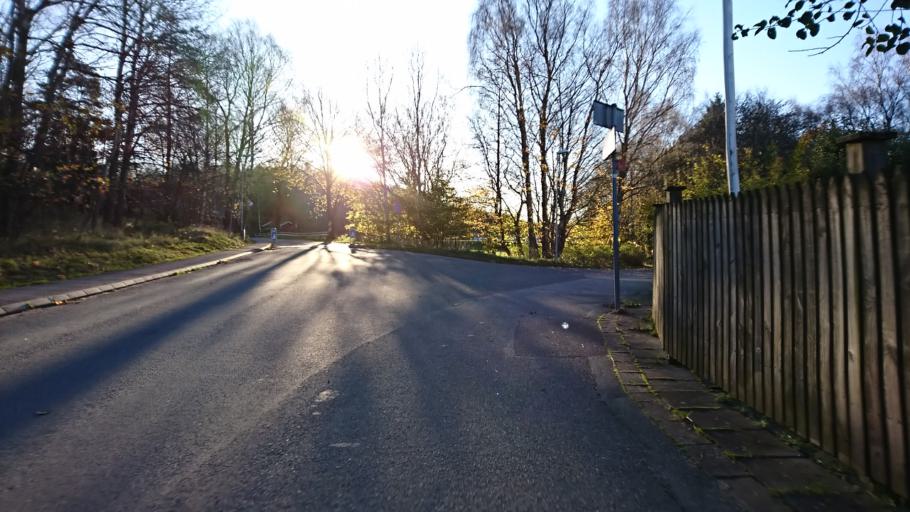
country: SE
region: Vaestra Goetaland
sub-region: Molndal
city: Moelndal
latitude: 57.6824
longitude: 12.0226
